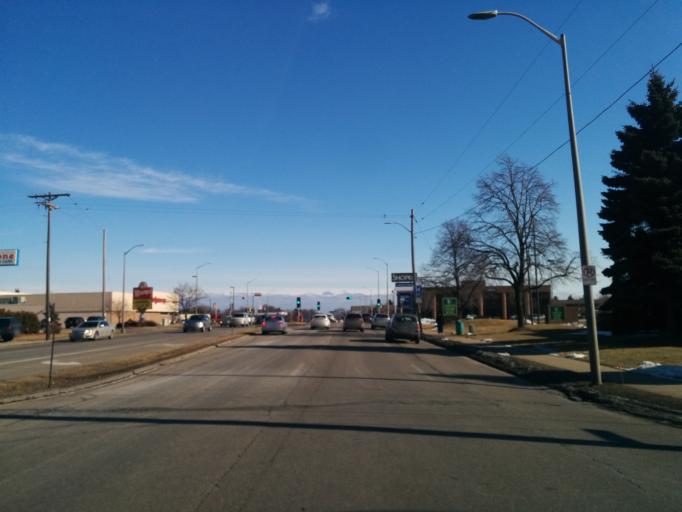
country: US
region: Wisconsin
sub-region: Racine County
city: Racine
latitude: 42.7186
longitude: -87.8394
